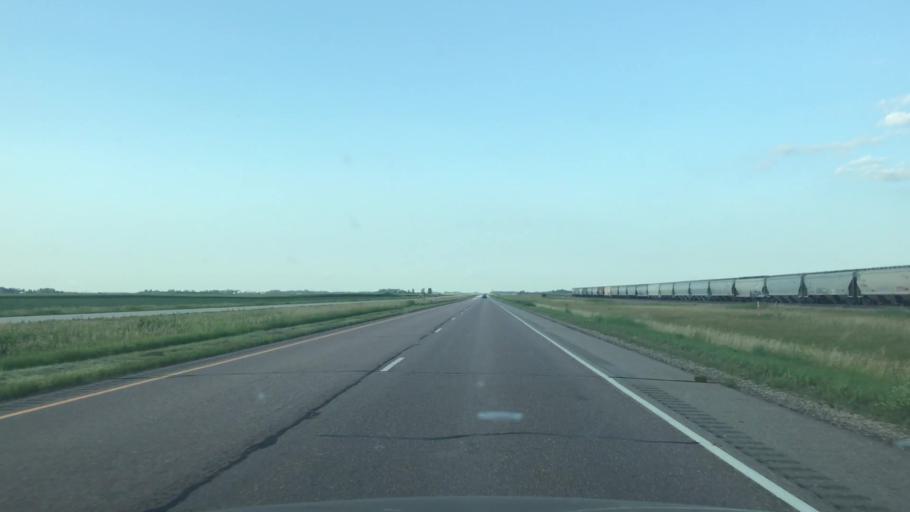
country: US
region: Minnesota
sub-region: Nobles County
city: Worthington
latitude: 43.7245
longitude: -95.4316
